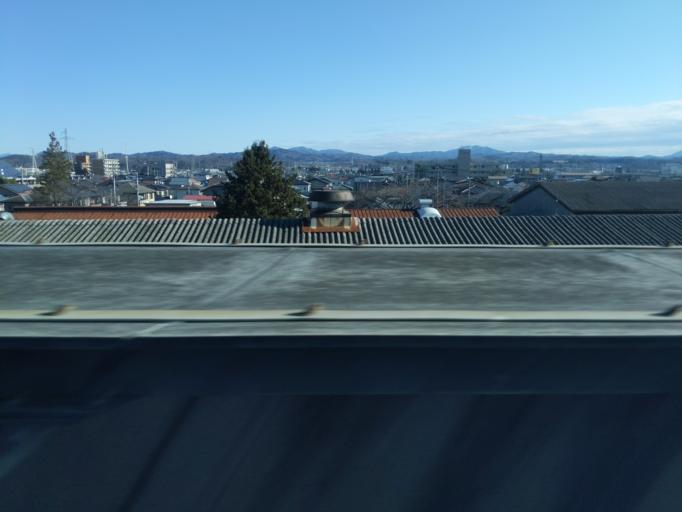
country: JP
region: Fukushima
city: Koriyama
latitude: 37.3864
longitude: 140.3858
